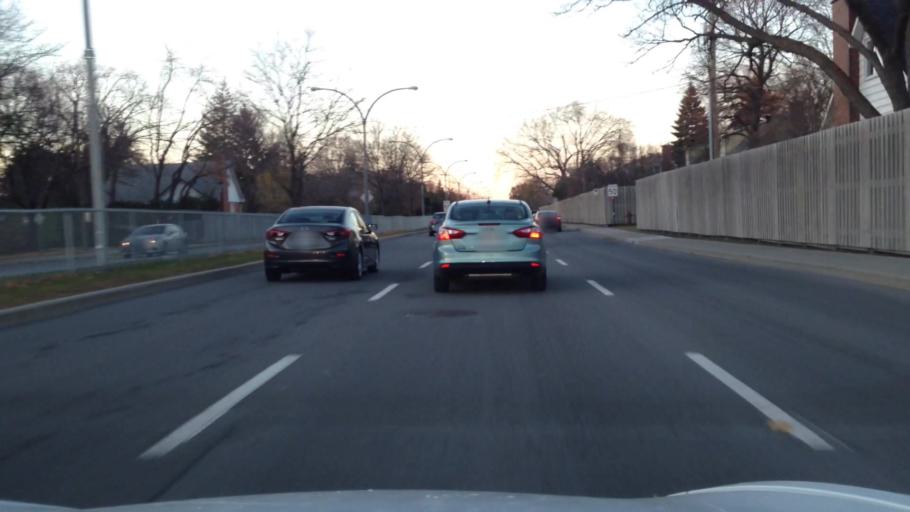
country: CA
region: Quebec
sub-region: Montreal
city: Pointe-Claire
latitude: 45.4508
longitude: -73.8185
